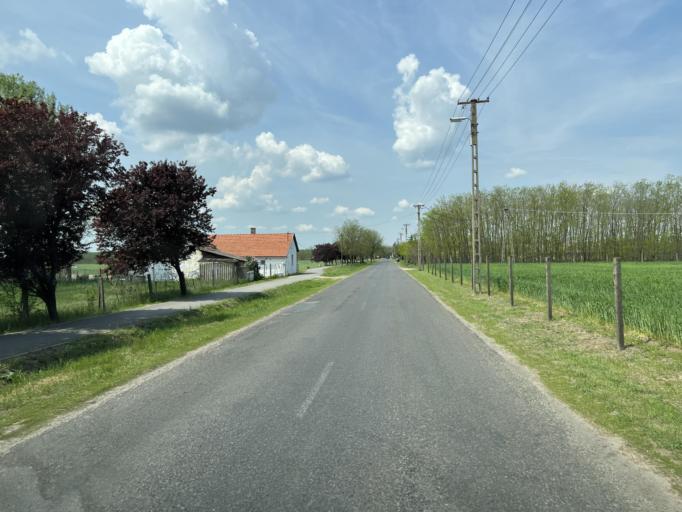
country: HU
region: Pest
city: Cegled
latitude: 47.1038
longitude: 19.7918
